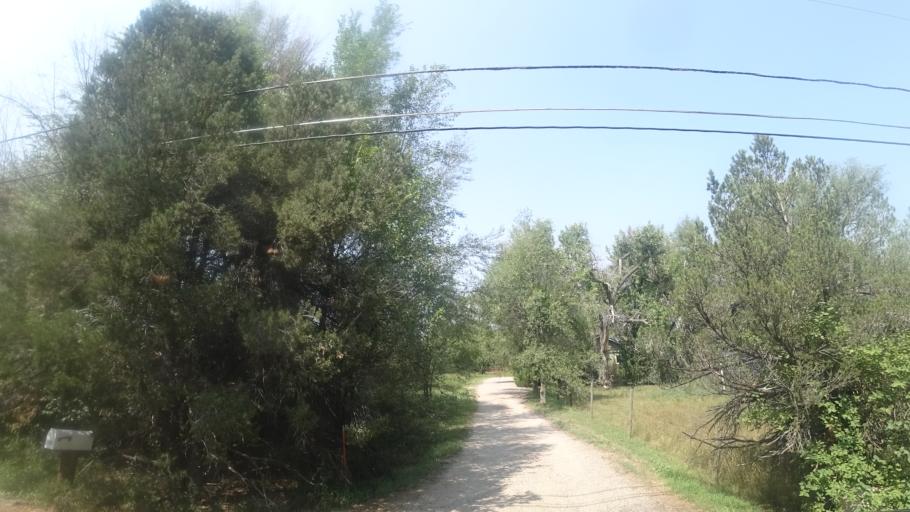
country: US
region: Colorado
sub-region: Arapahoe County
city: Cherry Hills Village
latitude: 39.6333
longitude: -104.9666
